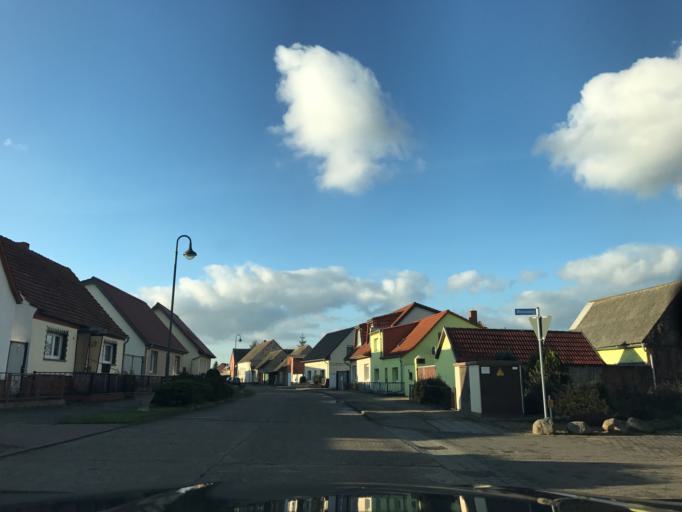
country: DE
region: Saxony-Anhalt
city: Loburg
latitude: 52.1801
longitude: 12.0440
